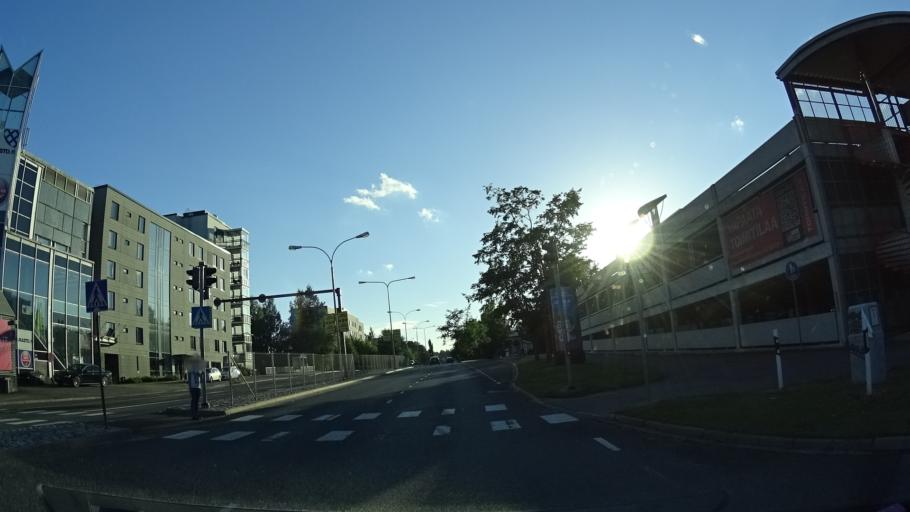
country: FI
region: Uusimaa
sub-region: Helsinki
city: Teekkarikylae
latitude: 60.2638
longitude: 24.8540
